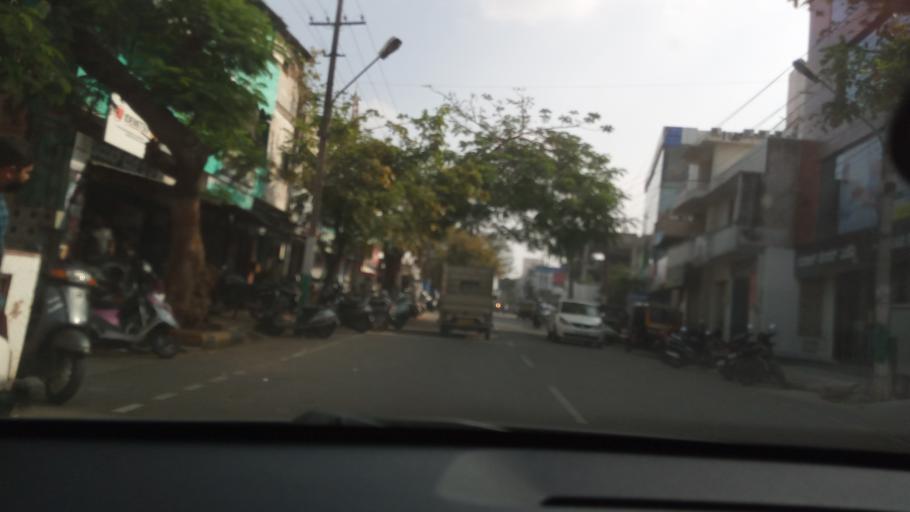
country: IN
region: Karnataka
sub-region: Mysore
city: Mysore
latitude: 12.3008
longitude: 76.6469
